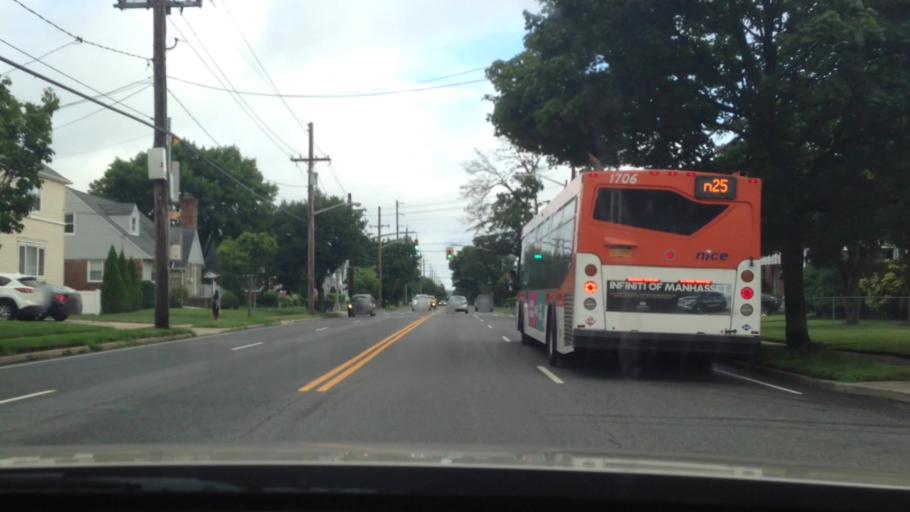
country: US
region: New York
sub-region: Nassau County
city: New Hyde Park
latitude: 40.7370
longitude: -73.6813
